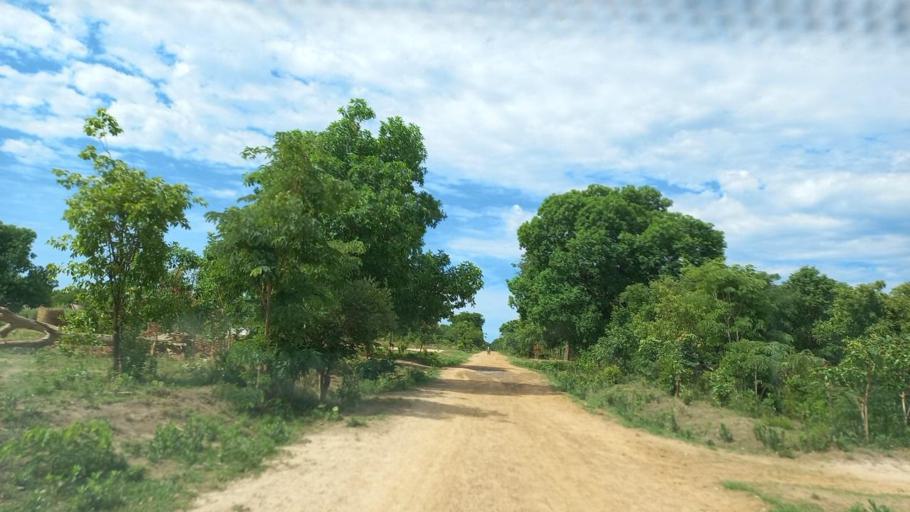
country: ZM
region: North-Western
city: Kabompo
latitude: -13.5206
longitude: 24.3849
